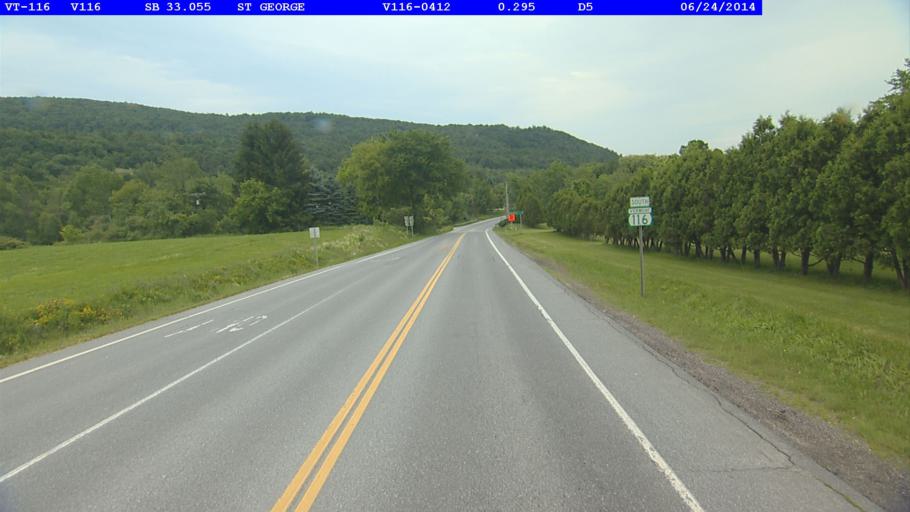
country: US
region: Vermont
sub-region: Chittenden County
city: Hinesburg
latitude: 44.3693
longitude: -73.1279
